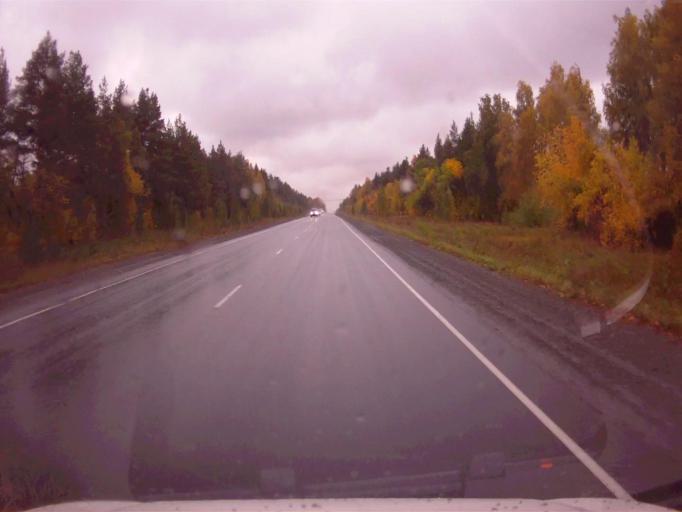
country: RU
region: Chelyabinsk
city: Roshchino
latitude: 55.3782
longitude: 61.1458
